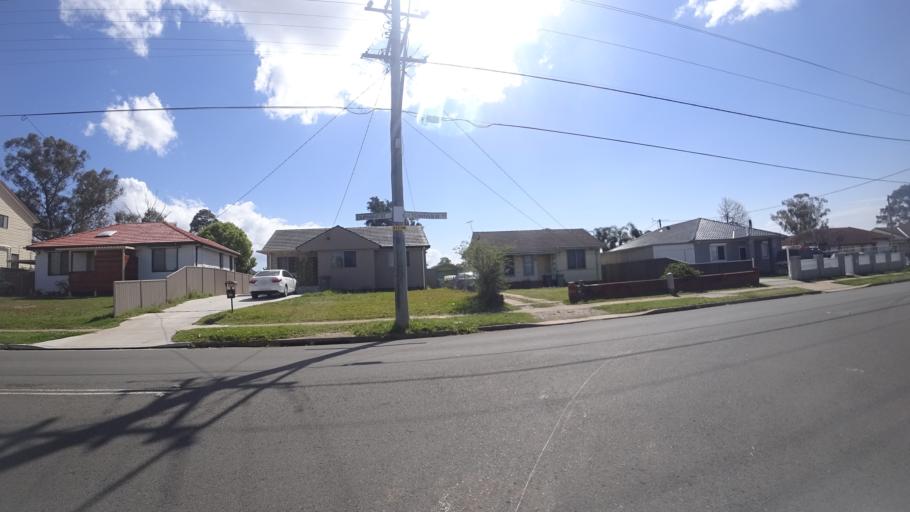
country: AU
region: New South Wales
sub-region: Fairfield
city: Cabramatta West
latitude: -33.8993
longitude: 150.9100
